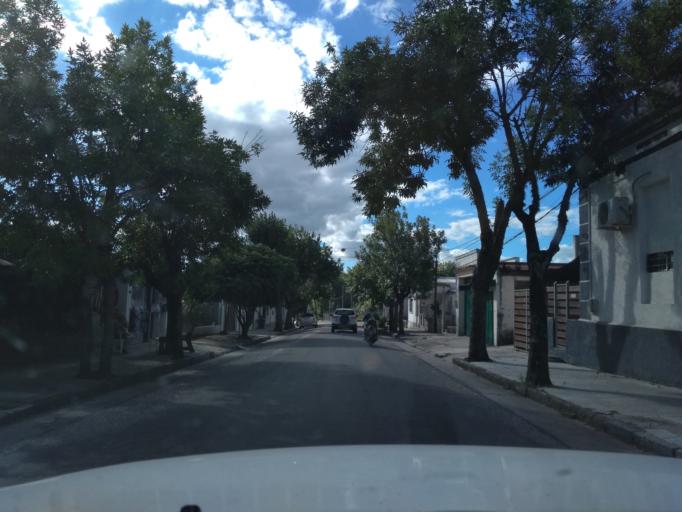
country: UY
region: Florida
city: Florida
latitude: -34.0948
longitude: -56.2221
